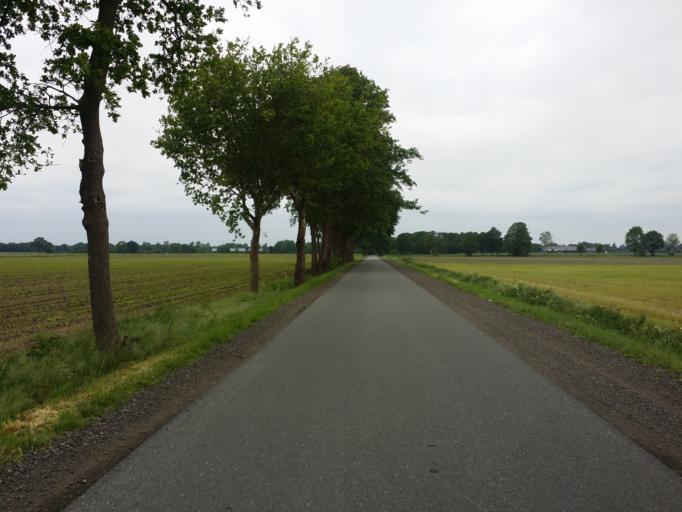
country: DE
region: Lower Saxony
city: Hatten
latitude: 53.1052
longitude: 8.3628
